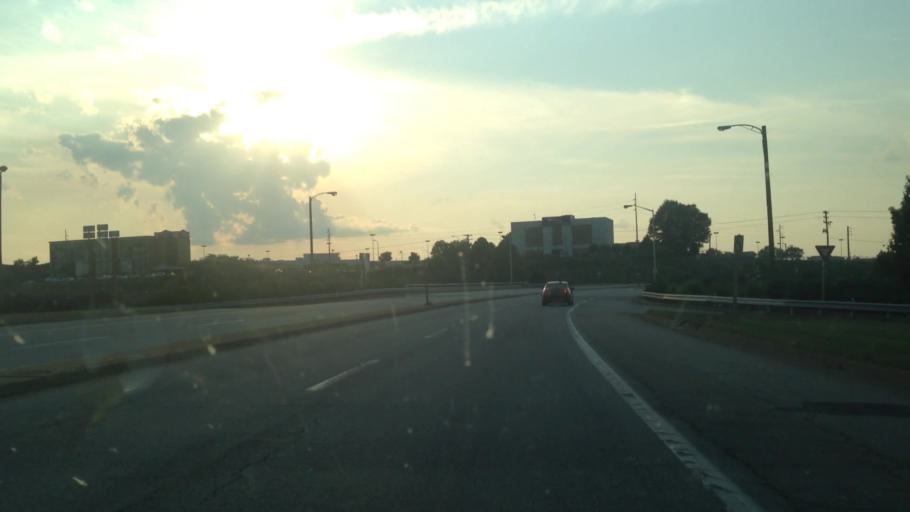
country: US
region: Virginia
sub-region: City of Danville
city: Danville
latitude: 36.5912
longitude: -79.4154
